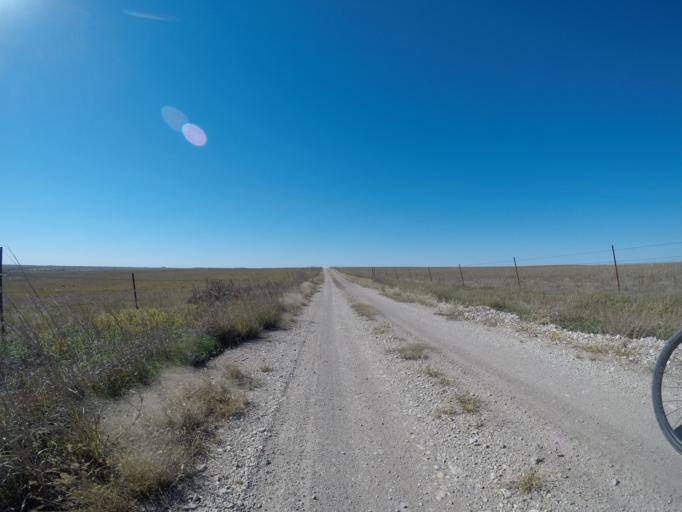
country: US
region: Kansas
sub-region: Wabaunsee County
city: Alma
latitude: 39.0290
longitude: -96.4042
